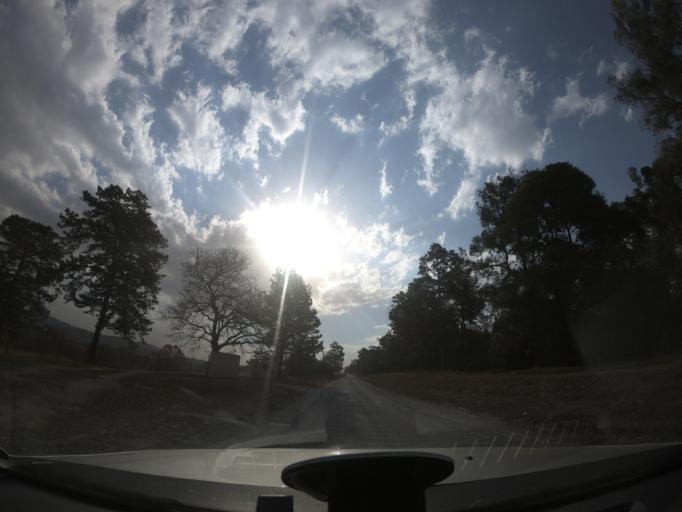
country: ZA
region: KwaZulu-Natal
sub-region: uMgungundlovu District Municipality
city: Howick
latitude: -29.4307
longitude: 30.1096
